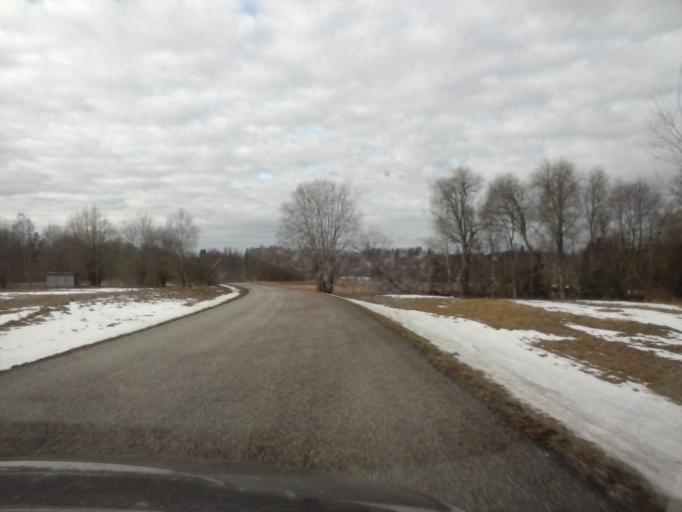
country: EE
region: Tartu
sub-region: Elva linn
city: Elva
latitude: 58.0139
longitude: 26.3035
